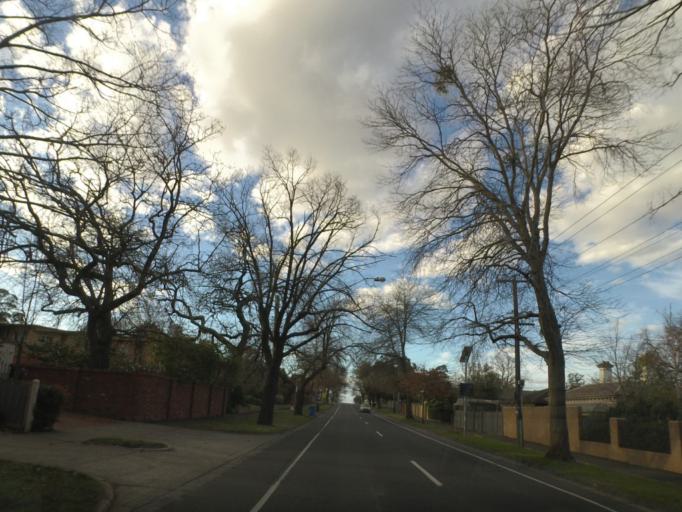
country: AU
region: Victoria
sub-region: Boroondara
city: Canterbury
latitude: -37.8168
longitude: 145.0805
